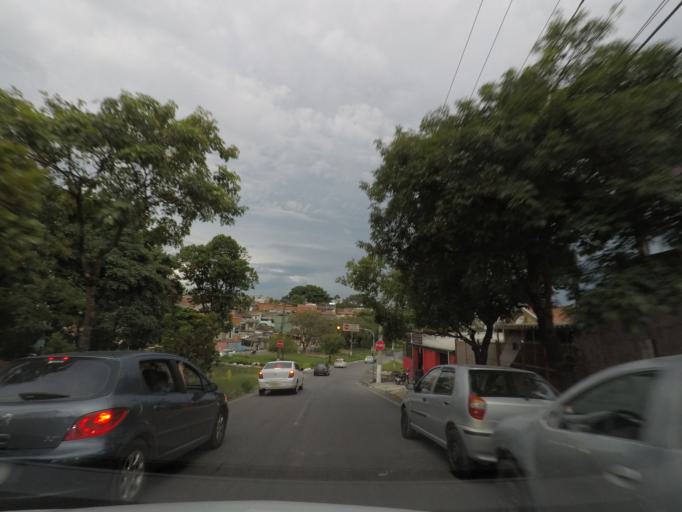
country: BR
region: Sao Paulo
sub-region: Campinas
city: Campinas
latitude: -22.9308
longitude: -47.1068
